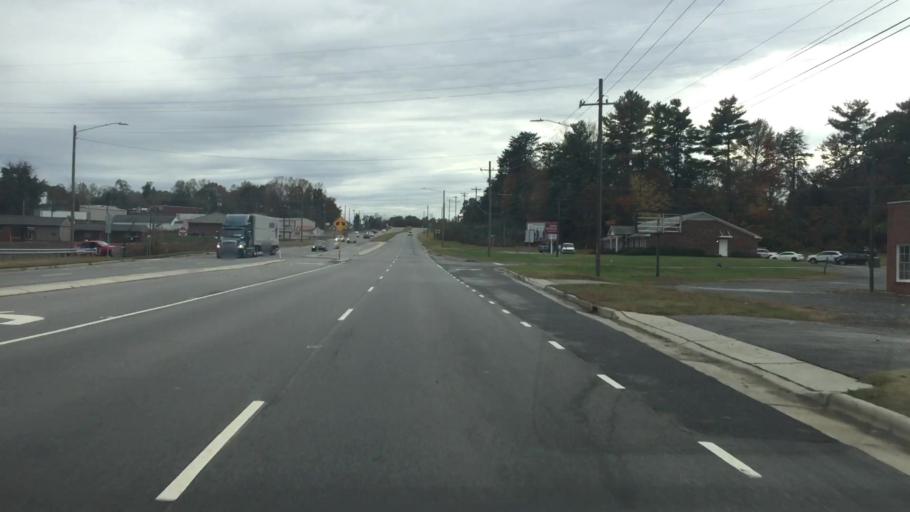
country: US
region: North Carolina
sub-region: Rockingham County
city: Reidsville
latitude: 36.3626
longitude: -79.6843
